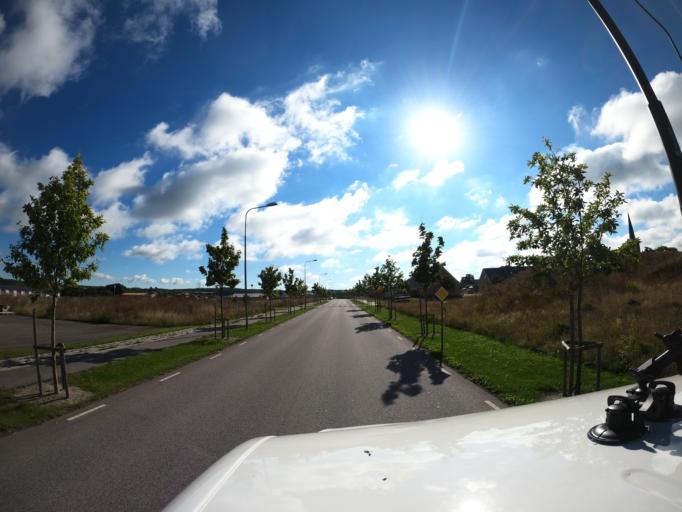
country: SE
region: Skane
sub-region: Lunds Kommun
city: Genarp
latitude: 55.6056
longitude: 13.3945
